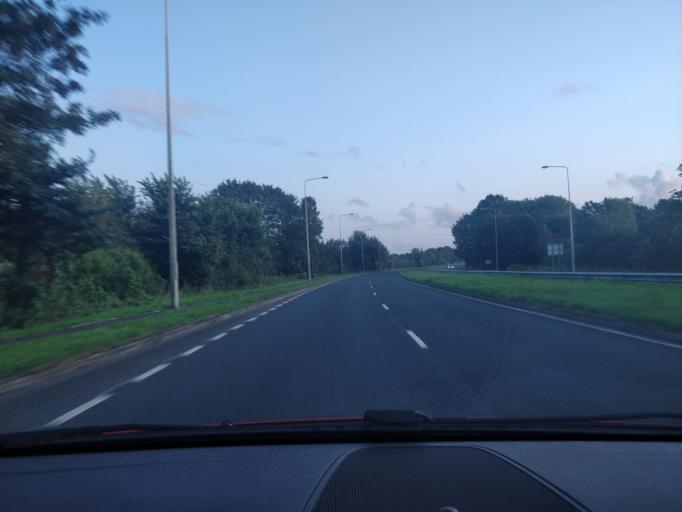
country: GB
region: England
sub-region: Lancashire
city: Preston
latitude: 53.7302
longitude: -2.7598
